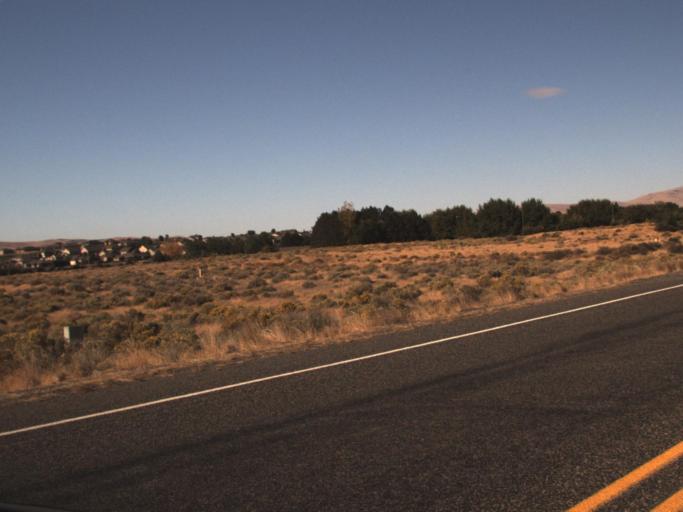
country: US
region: Washington
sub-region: Benton County
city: Richland
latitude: 46.3239
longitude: -119.3131
